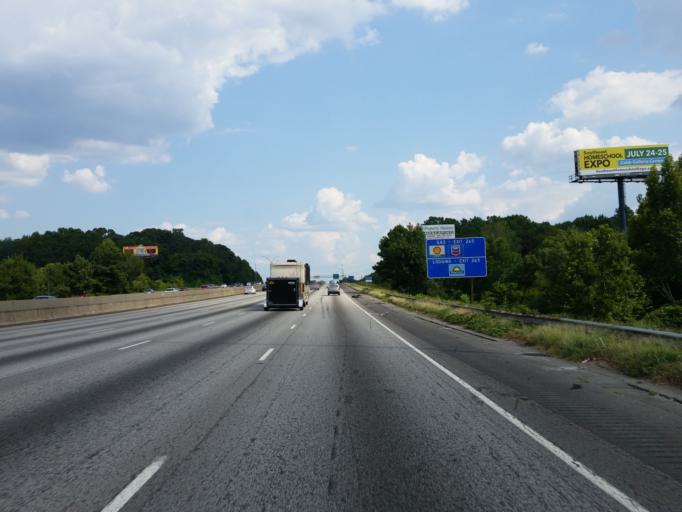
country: US
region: Georgia
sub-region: Cobb County
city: Marietta
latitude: 33.9687
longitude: -84.5269
